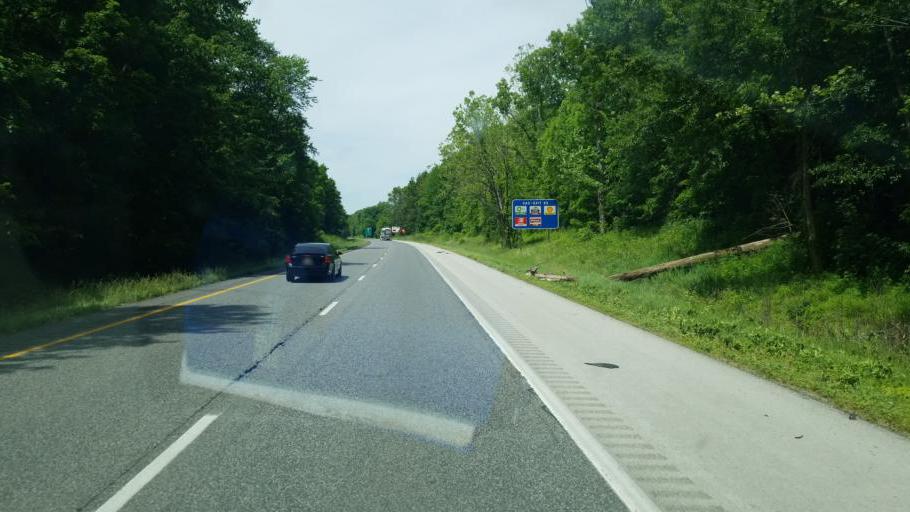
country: US
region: Indiana
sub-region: Clay County
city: Brazil
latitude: 39.4560
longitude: -87.0968
